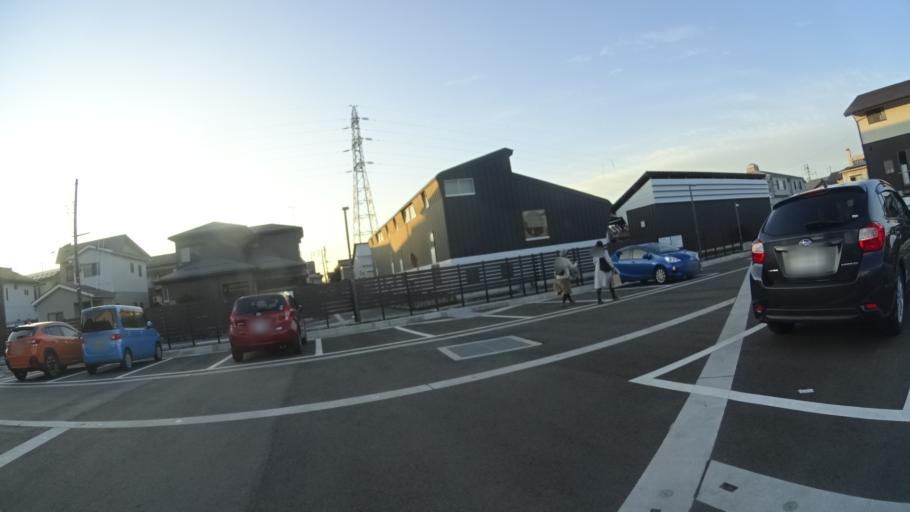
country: JP
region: Niigata
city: Nagaoka
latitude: 37.4165
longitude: 138.8403
